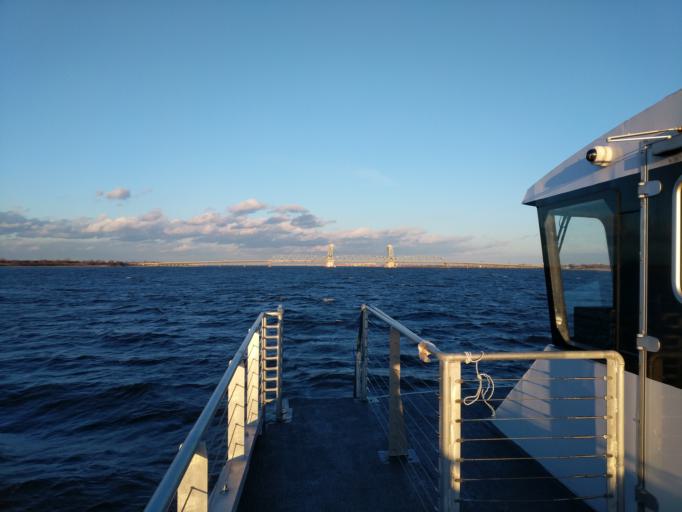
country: US
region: New York
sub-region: Kings County
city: Brooklyn
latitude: 40.5708
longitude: -73.9016
